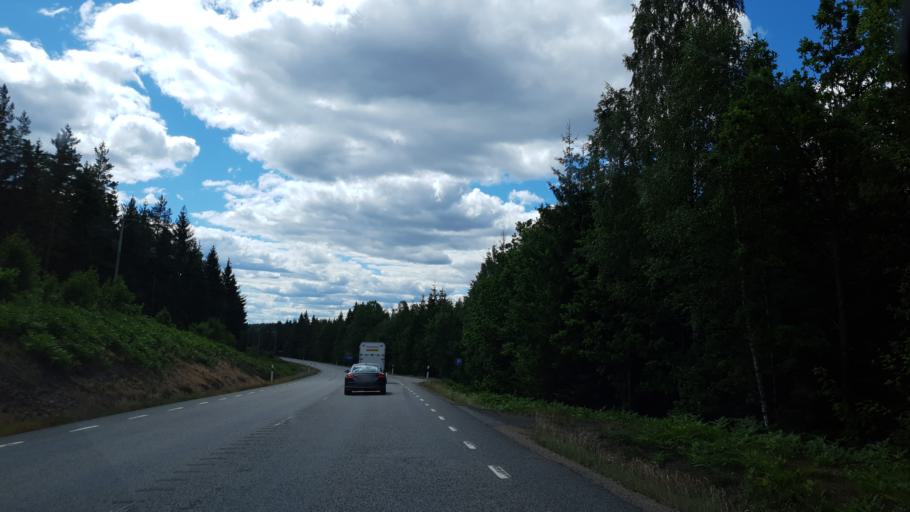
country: SE
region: Kronoberg
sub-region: Vaxjo Kommun
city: Braas
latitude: 57.1547
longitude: 15.1588
